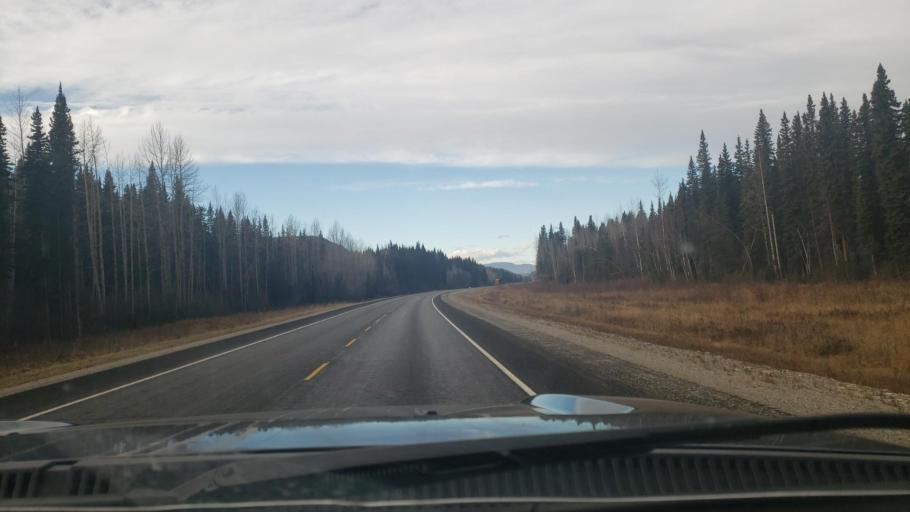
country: CA
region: British Columbia
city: Fort Nelson
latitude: 58.6547
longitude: -124.1511
